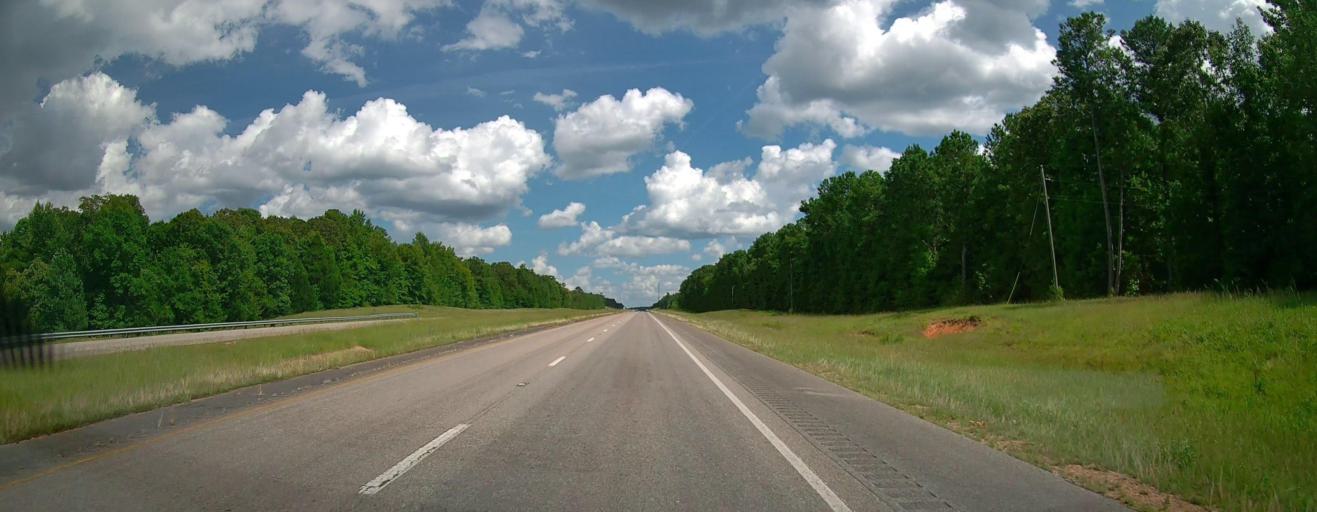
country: US
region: Mississippi
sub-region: Lowndes County
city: New Hope
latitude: 33.4635
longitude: -88.2282
